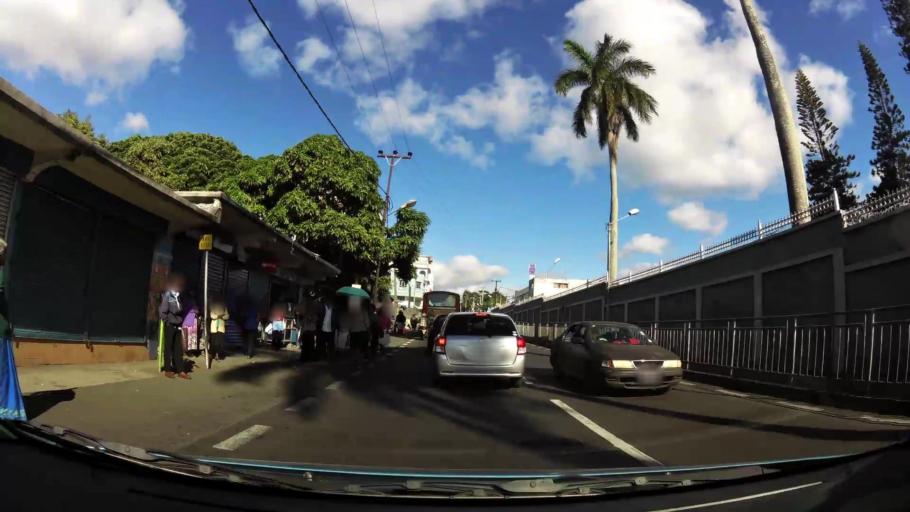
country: MU
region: Plaines Wilhems
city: Quatre Bornes
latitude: -20.2775
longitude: 57.4773
